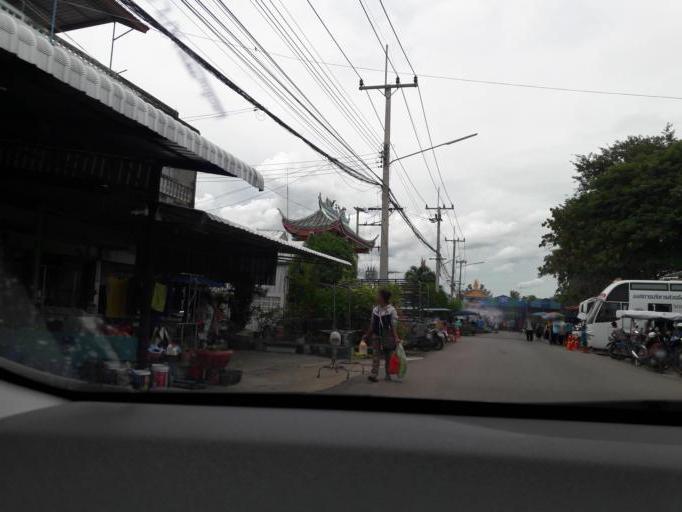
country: TH
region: Samut Sakhon
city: Ban Phaeo
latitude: 13.5557
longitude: 100.0429
